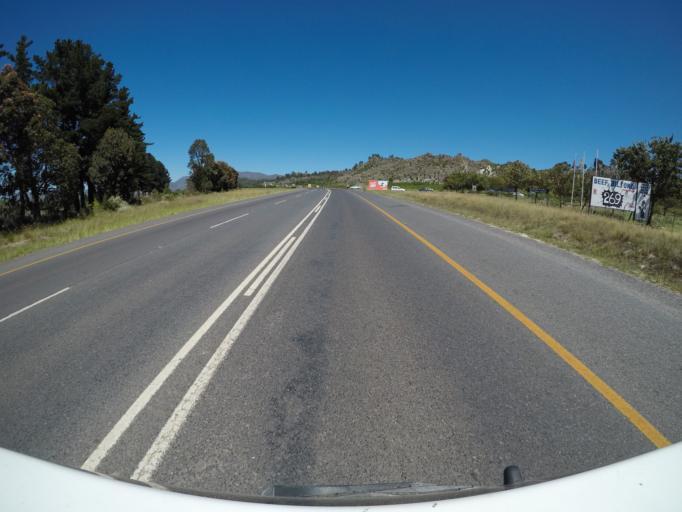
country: ZA
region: Western Cape
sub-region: Overberg District Municipality
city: Grabouw
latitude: -34.1627
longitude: 19.0098
